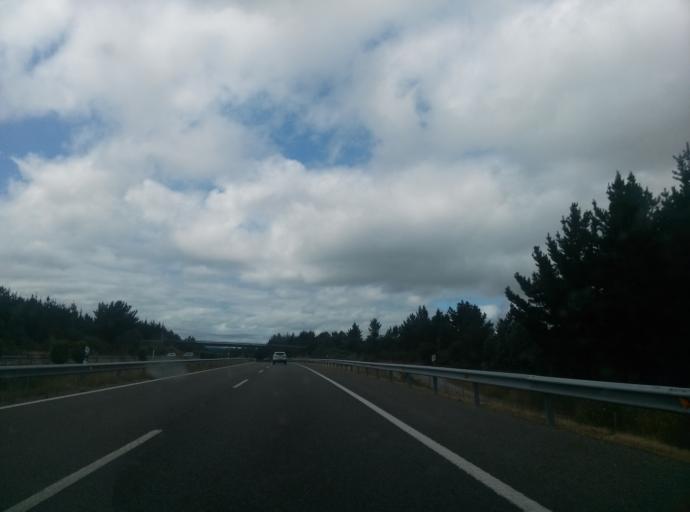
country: ES
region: Galicia
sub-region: Provincia de Lugo
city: Outeiro de Rei
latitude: 43.0902
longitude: -7.5858
